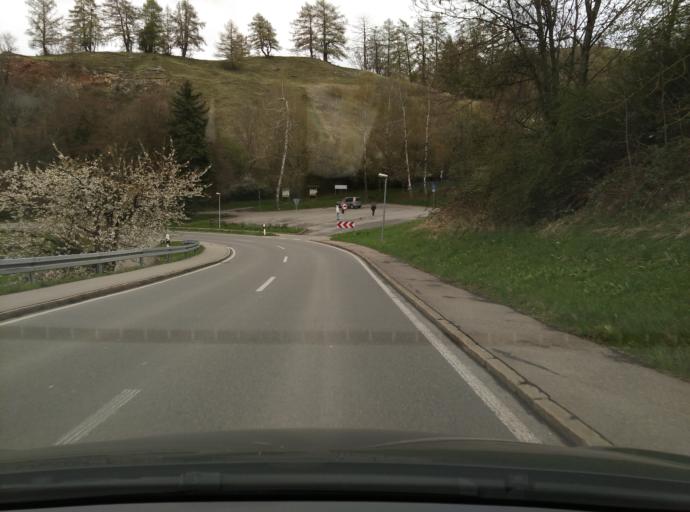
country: DE
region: Baden-Wuerttemberg
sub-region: Regierungsbezirk Stuttgart
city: Kohlberg
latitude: 48.5533
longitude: 9.3292
